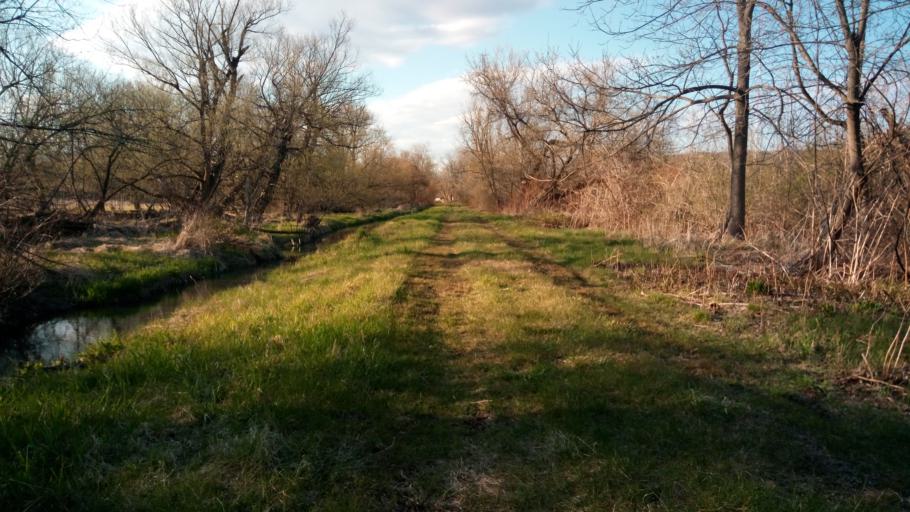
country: US
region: New York
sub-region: Chemung County
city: Elmira Heights
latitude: 42.1186
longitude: -76.8111
